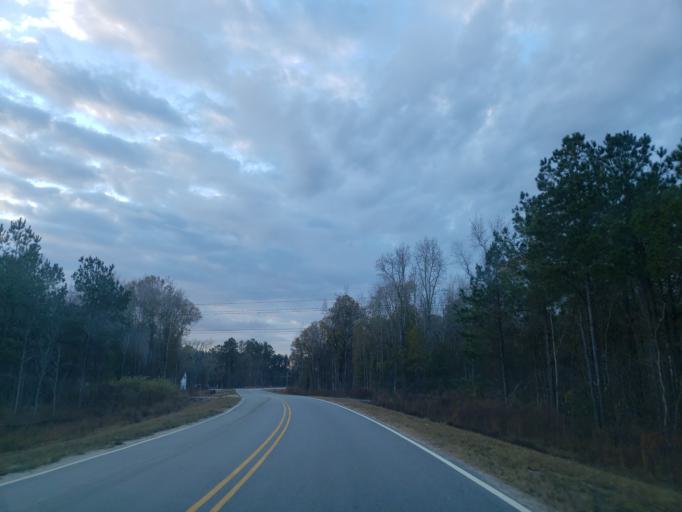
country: US
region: Georgia
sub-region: Chatham County
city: Bloomingdale
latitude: 32.1331
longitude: -81.3161
